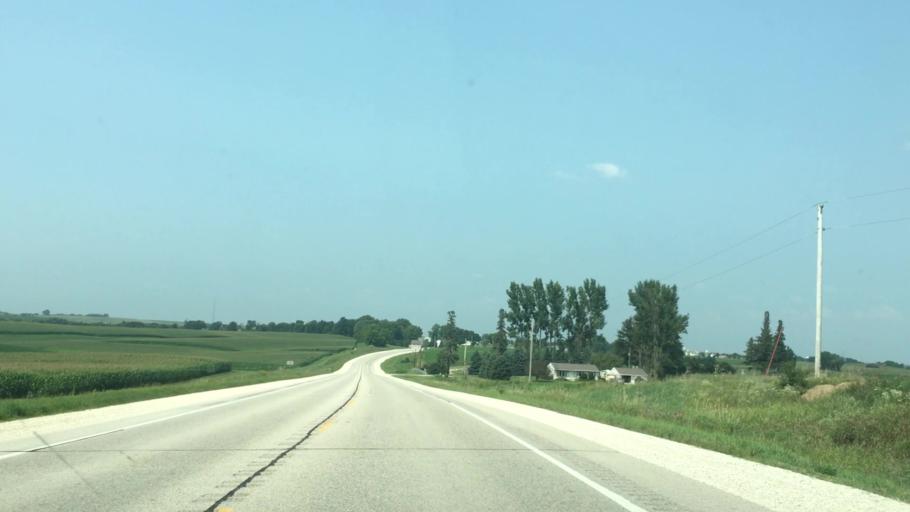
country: US
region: Iowa
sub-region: Winneshiek County
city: Decorah
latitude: 43.2559
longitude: -91.8383
